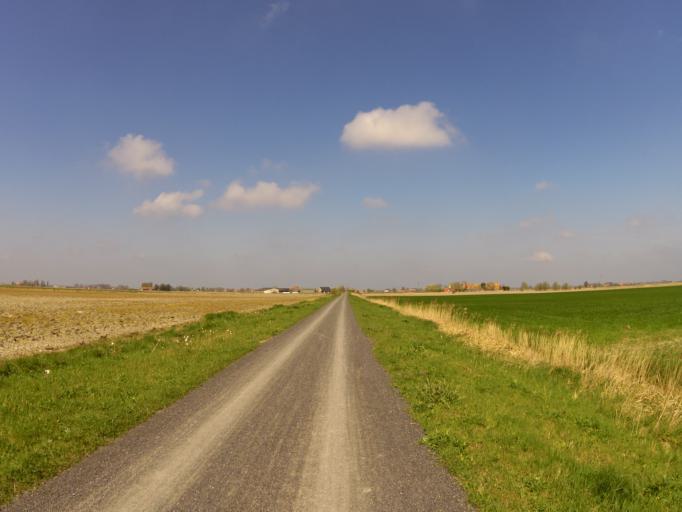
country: BE
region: Flanders
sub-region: Provincie West-Vlaanderen
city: Diksmuide
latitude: 51.0598
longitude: 2.8134
